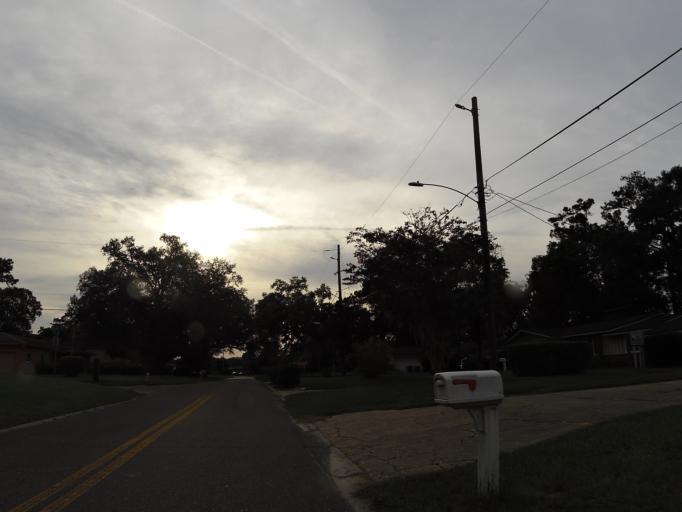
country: US
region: Florida
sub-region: Duval County
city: Jacksonville
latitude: 30.3980
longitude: -81.7007
